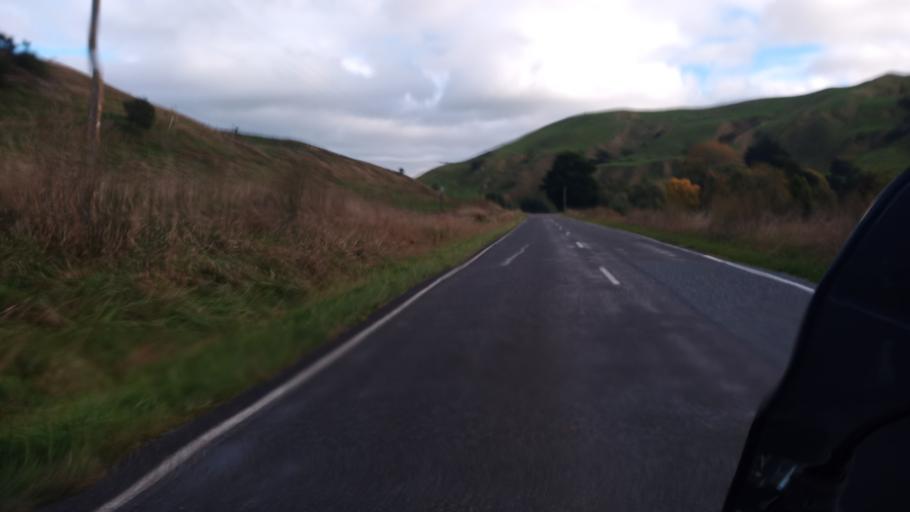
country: NZ
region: Gisborne
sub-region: Gisborne District
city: Gisborne
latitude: -38.5743
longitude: 177.7377
